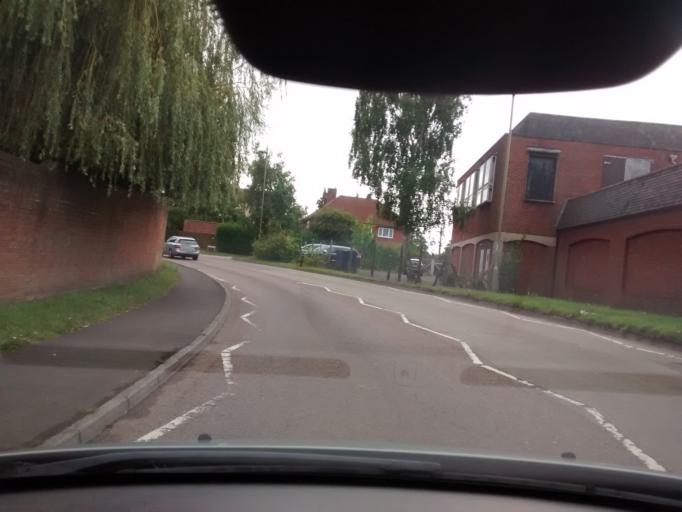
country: GB
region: England
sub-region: Hampshire
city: Ringwood
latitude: 50.8469
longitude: -1.7901
